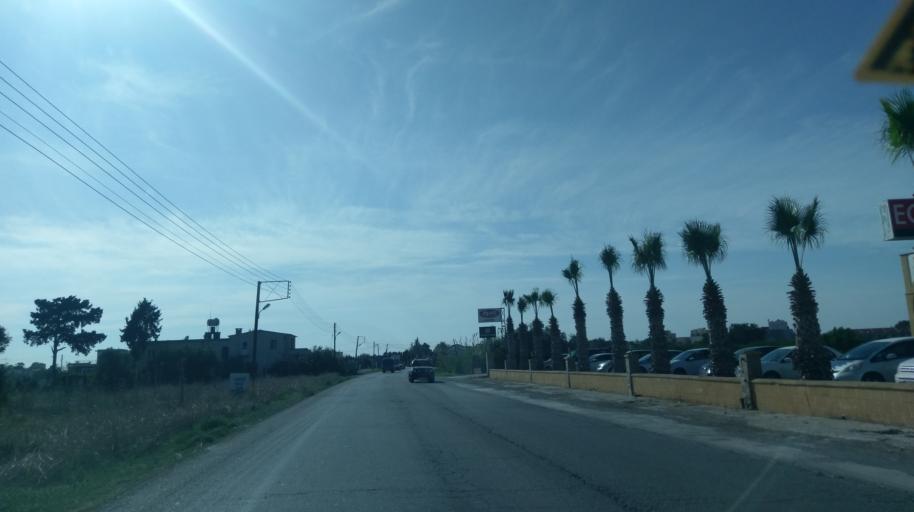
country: CY
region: Ammochostos
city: Trikomo
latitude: 35.2874
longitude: 33.9289
